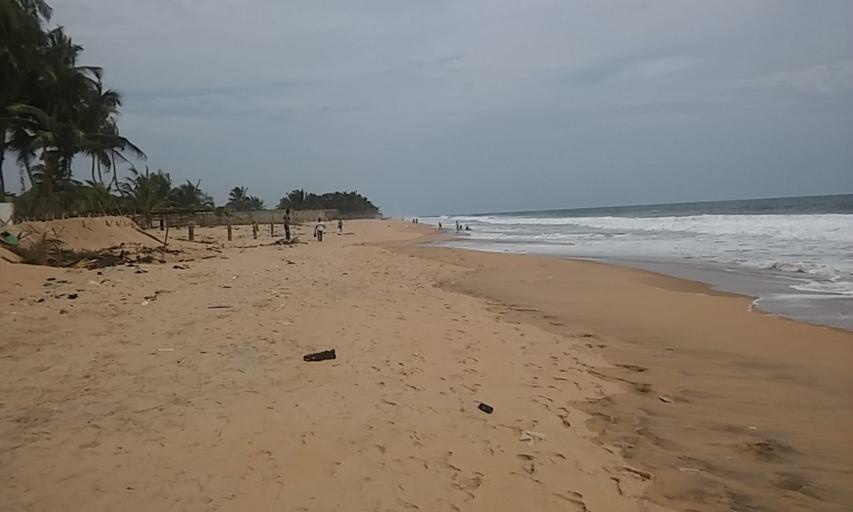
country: CI
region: Sud-Comoe
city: Grand-Bassam
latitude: 5.1934
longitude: -3.7327
